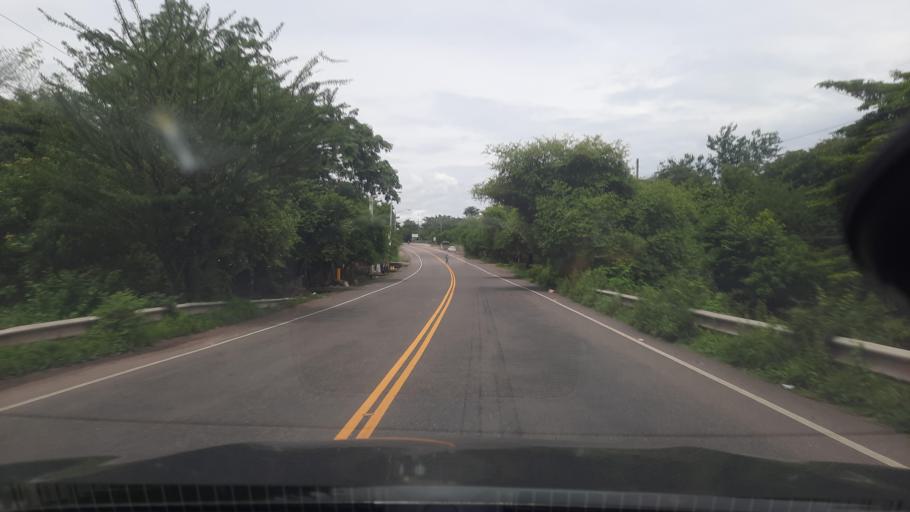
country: HN
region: Valle
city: Jicaro Galan
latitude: 13.5340
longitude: -87.4617
